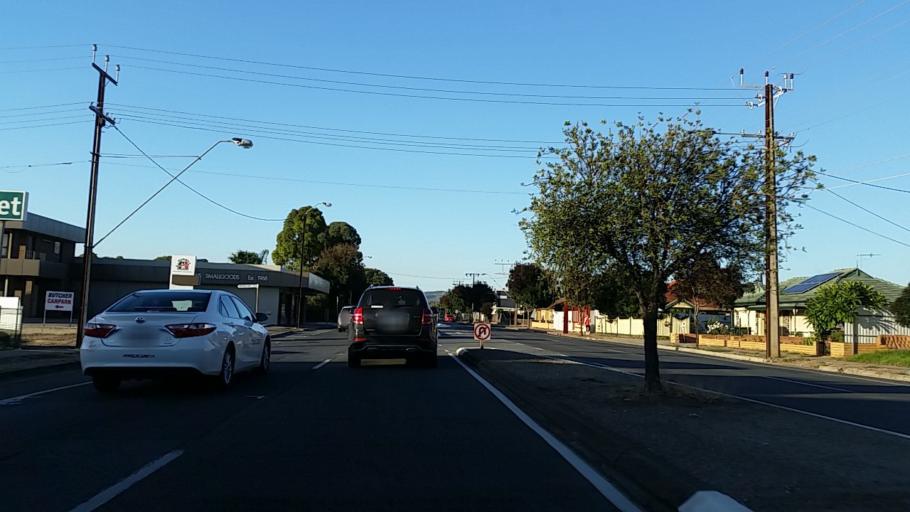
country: AU
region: South Australia
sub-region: Campbelltown
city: Paradise
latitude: -34.8754
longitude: 138.6663
